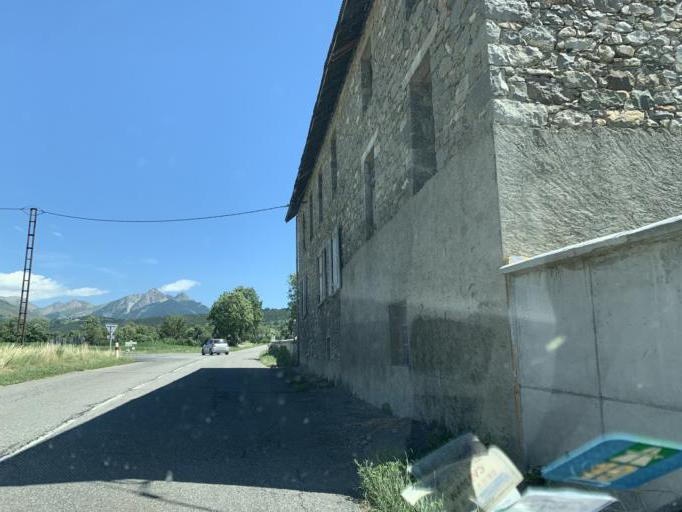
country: FR
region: Provence-Alpes-Cote d'Azur
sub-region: Departement des Hautes-Alpes
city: Saint-Bonnet-en-Champsaur
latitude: 44.6425
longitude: 6.1355
